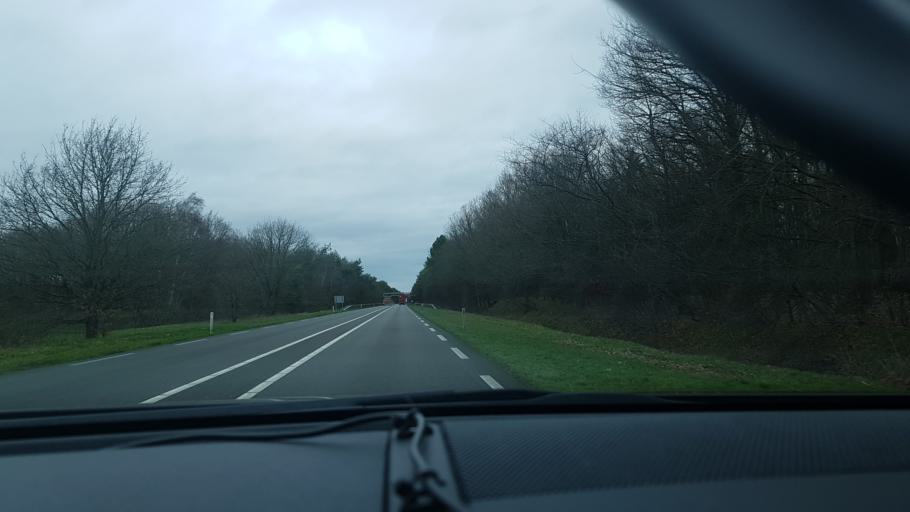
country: NL
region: North Brabant
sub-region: Gemeente Asten
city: Asten
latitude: 51.4400
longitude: 5.7336
